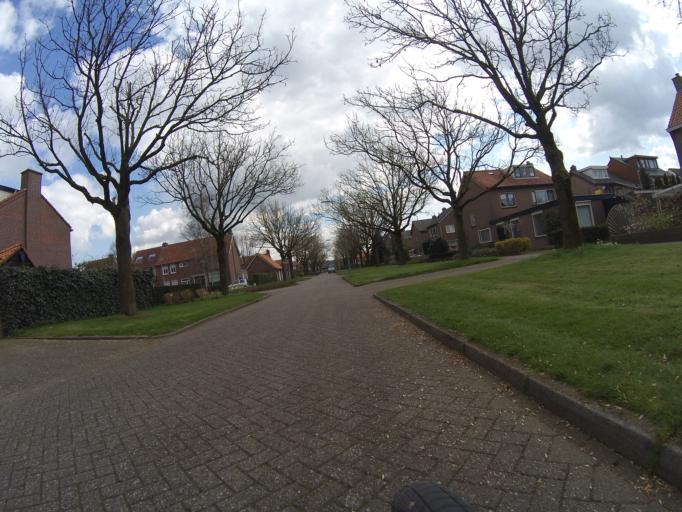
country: NL
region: Gelderland
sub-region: Gemeente Barneveld
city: Zwartebroek
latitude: 52.1742
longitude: 5.4597
